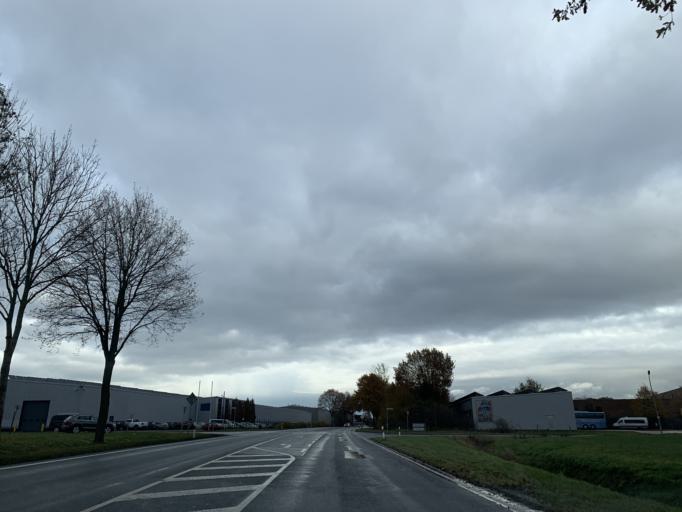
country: NL
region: Overijssel
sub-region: Gemeente Enschede
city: Enschede
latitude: 52.1349
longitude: 6.9111
